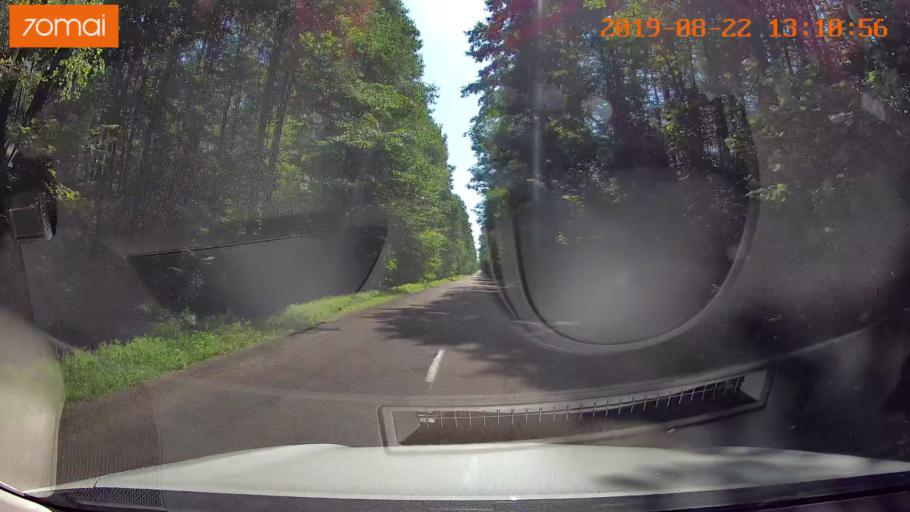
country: BY
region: Minsk
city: Prawdzinski
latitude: 53.2876
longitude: 27.8509
